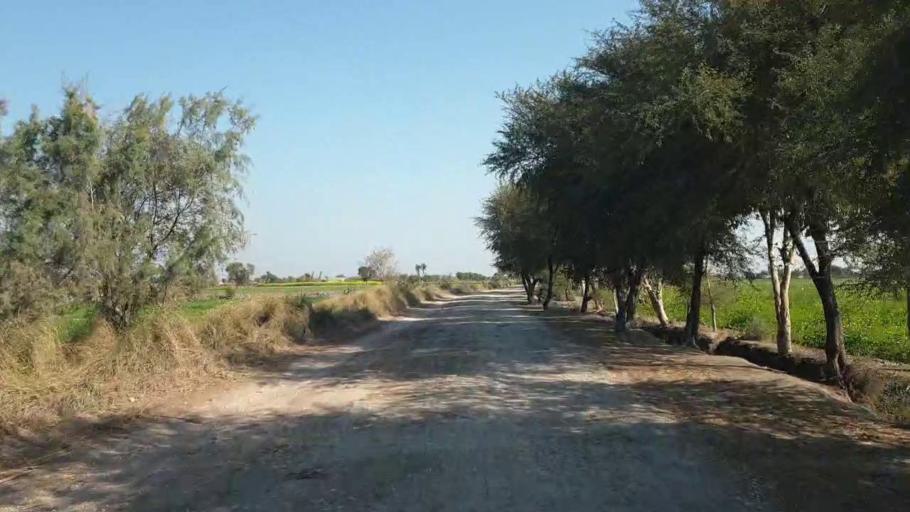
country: PK
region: Sindh
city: Shahdadpur
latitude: 25.9787
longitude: 68.6741
